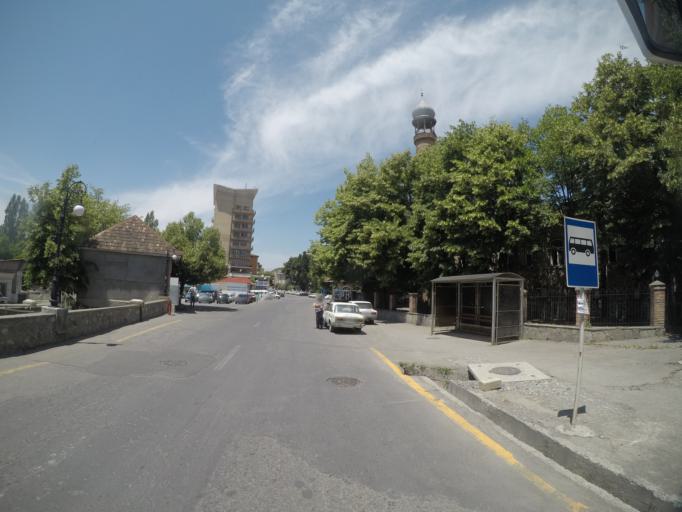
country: AZ
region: Shaki City
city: Sheki
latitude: 41.2021
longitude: 47.1813
